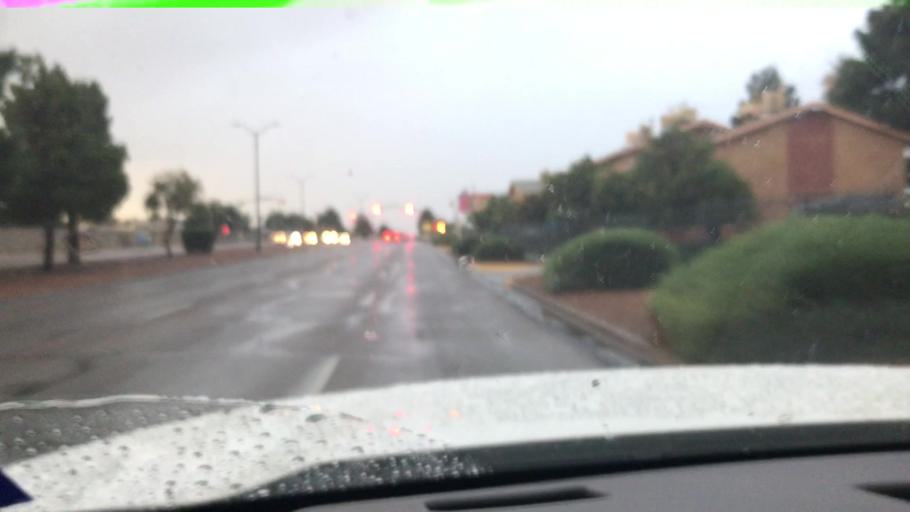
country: US
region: Texas
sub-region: El Paso County
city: Fort Bliss
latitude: 31.7929
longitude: -106.3234
